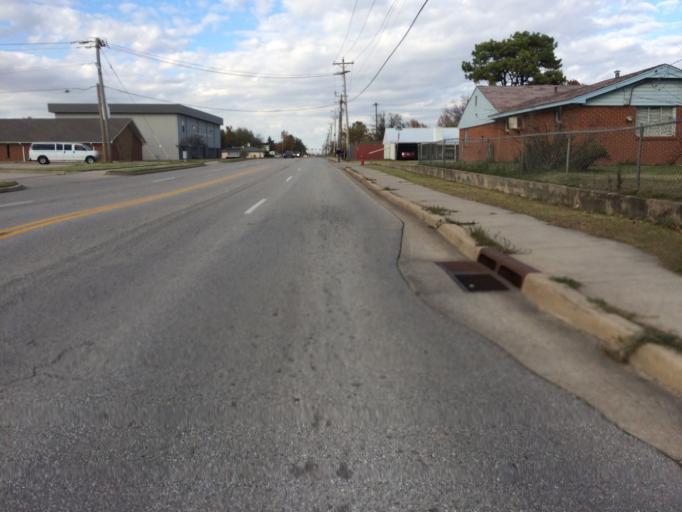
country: US
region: Oklahoma
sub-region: Cleveland County
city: Norman
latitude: 35.2348
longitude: -97.4499
